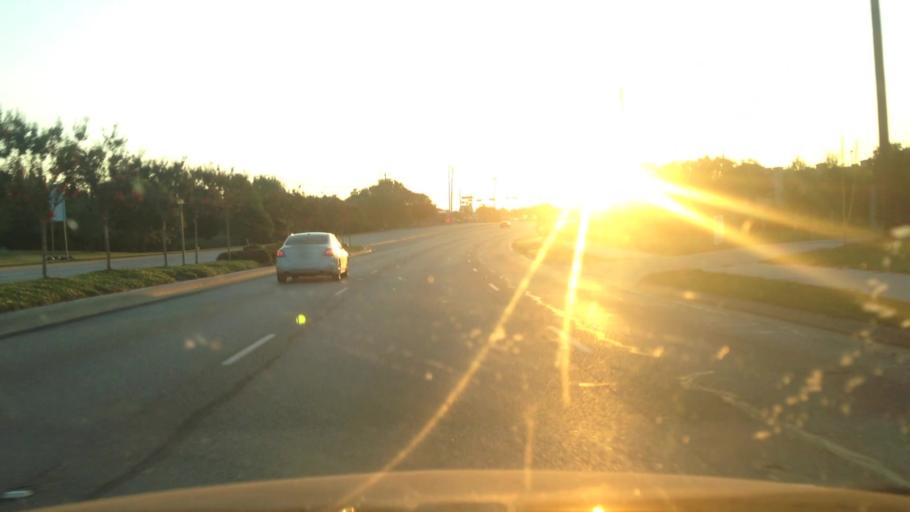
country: US
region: Texas
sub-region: Tarrant County
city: Southlake
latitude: 32.9409
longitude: -97.1800
